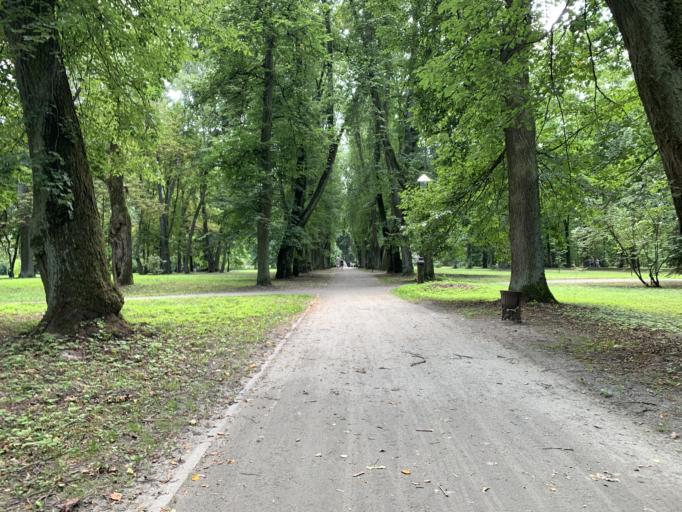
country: BY
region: Minsk
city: Nyasvizh
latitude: 53.2271
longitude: 26.6939
